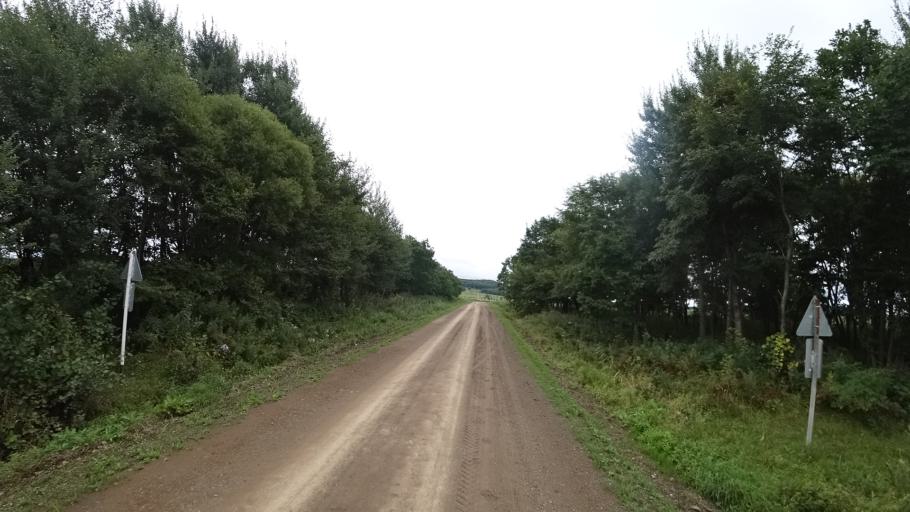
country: RU
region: Primorskiy
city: Chernigovka
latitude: 44.4796
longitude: 132.5763
